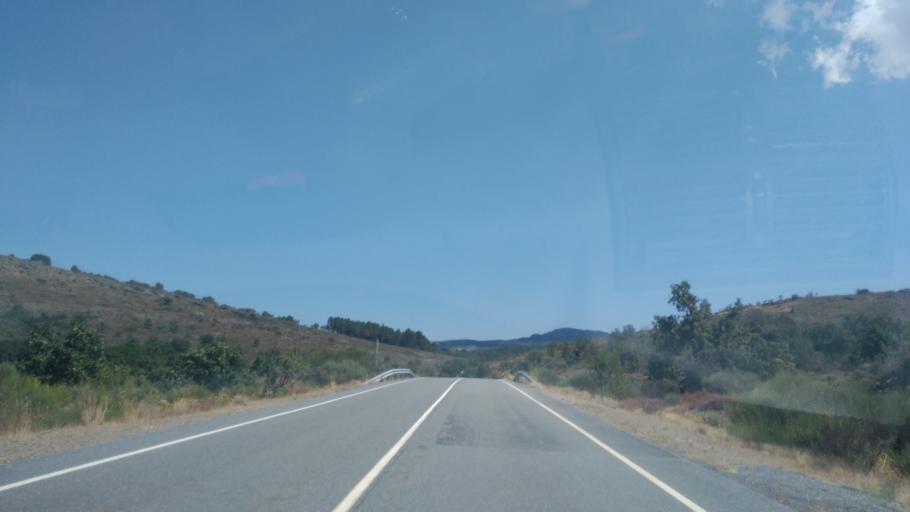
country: ES
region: Castille and Leon
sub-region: Provincia de Salamanca
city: Cereceda de la Sierra
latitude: 40.5773
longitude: -6.0799
